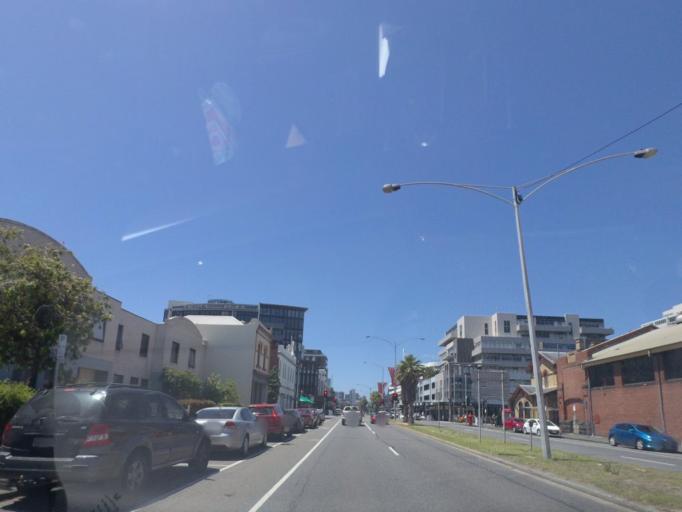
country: AU
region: Victoria
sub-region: Port Phillip
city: Port Melbourne
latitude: -37.8425
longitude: 144.9386
